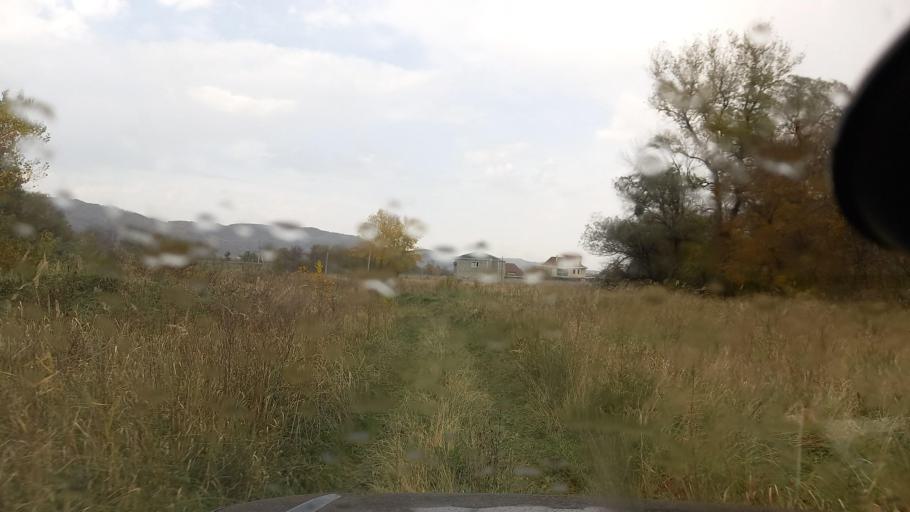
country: RU
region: Krasnodarskiy
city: Shedok
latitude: 44.1725
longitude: 40.8447
